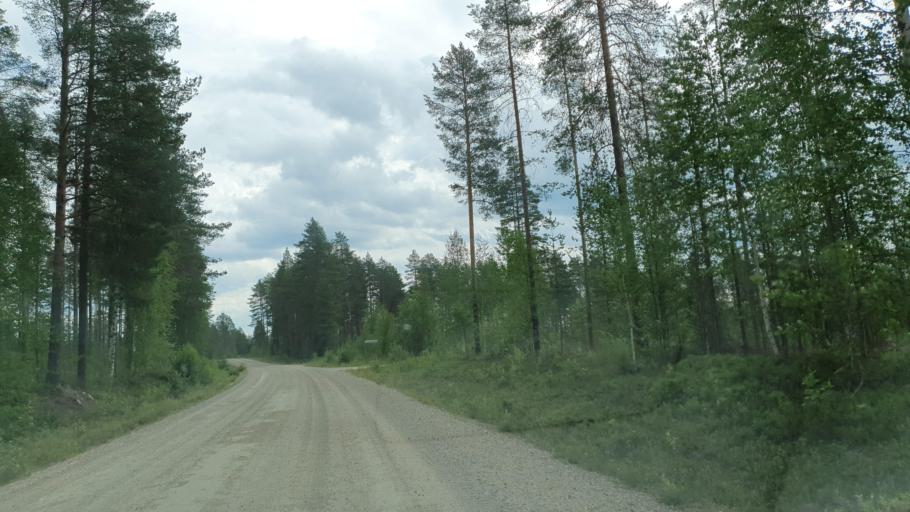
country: FI
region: Kainuu
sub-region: Kehys-Kainuu
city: Kuhmo
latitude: 64.7230
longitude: 29.6858
